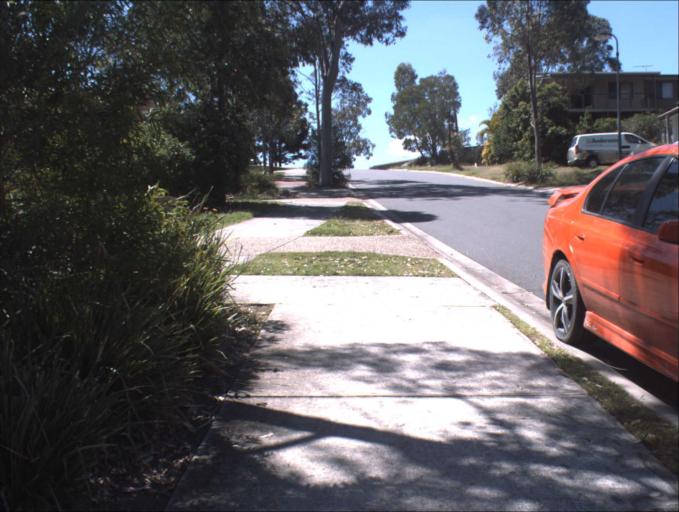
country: AU
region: Queensland
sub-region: Logan
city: Waterford West
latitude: -27.7092
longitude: 153.1571
